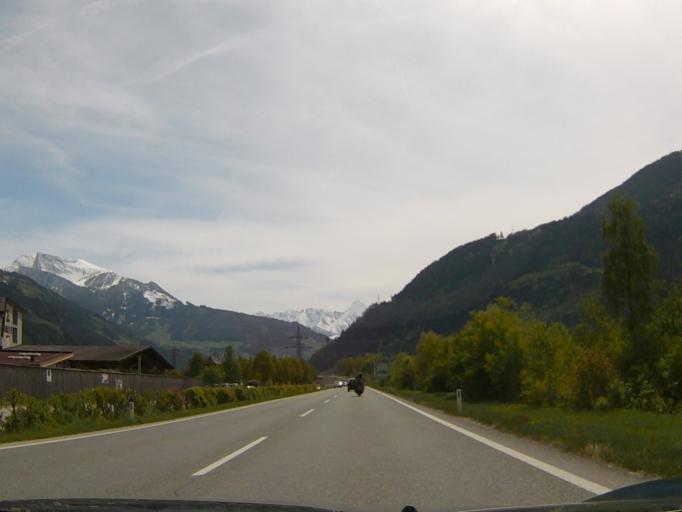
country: AT
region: Tyrol
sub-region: Politischer Bezirk Schwaz
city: Stummerberg
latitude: 47.2673
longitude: 11.9003
